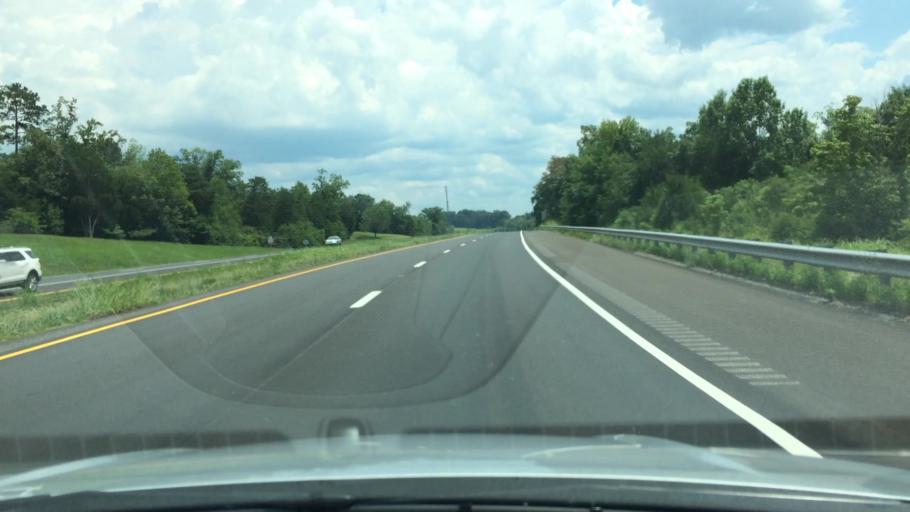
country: US
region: Tennessee
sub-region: Hamblen County
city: Morristown
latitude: 36.1804
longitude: -83.2349
